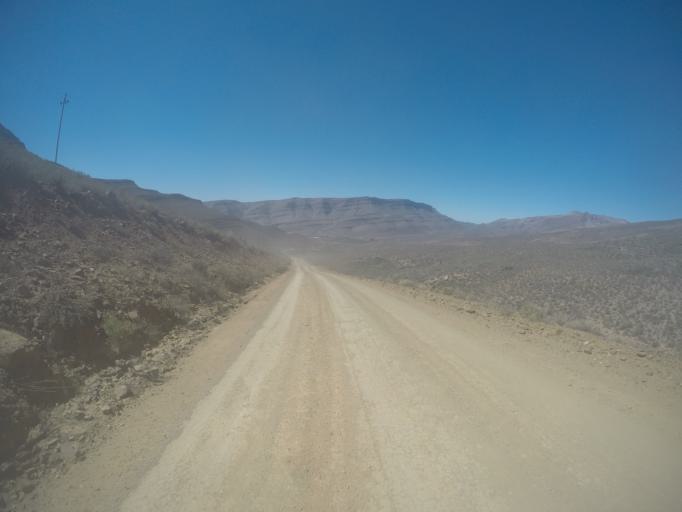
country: ZA
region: Western Cape
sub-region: West Coast District Municipality
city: Clanwilliam
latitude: -32.6175
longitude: 19.3771
